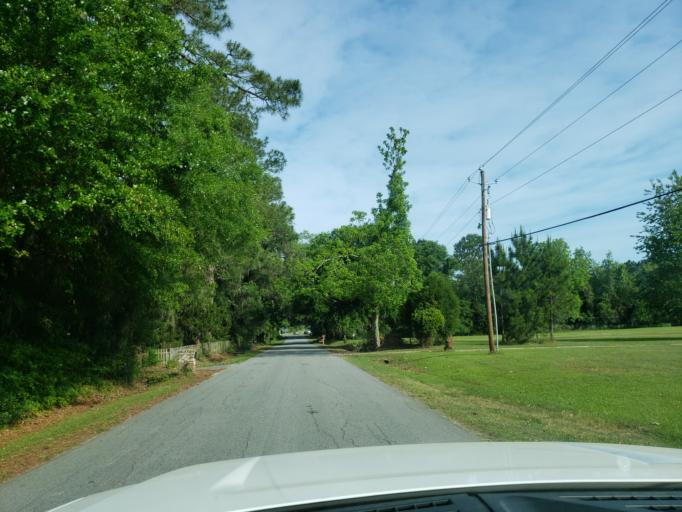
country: US
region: Georgia
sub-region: Chatham County
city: Georgetown
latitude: 32.0103
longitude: -81.2325
